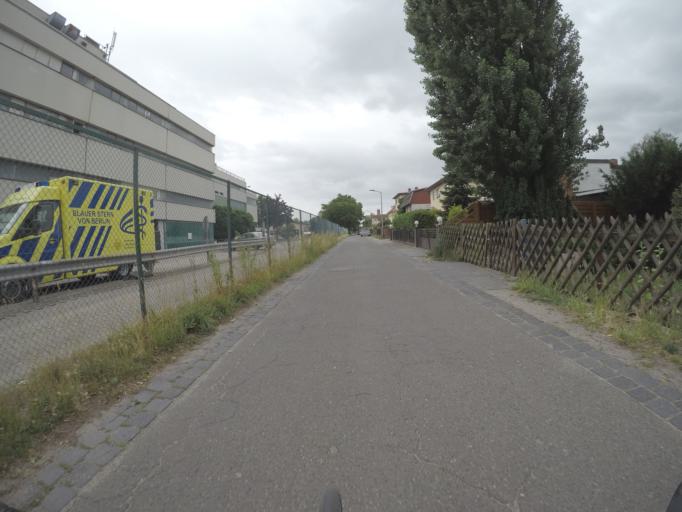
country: DE
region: Berlin
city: Mariendorf
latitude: 52.4294
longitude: 13.3872
